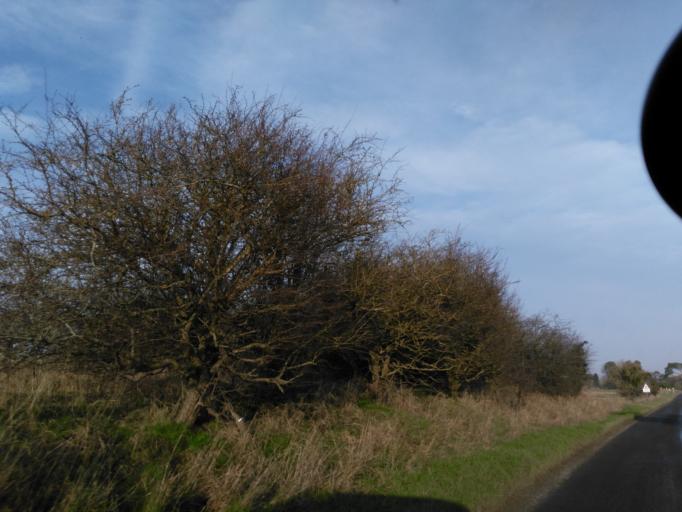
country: GB
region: England
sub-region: Wiltshire
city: Market Lavington
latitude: 51.2366
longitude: -1.9719
